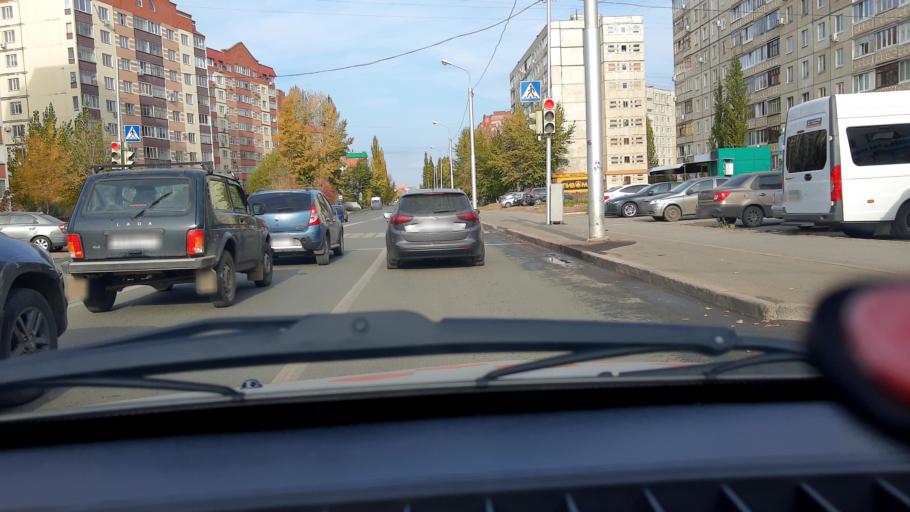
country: RU
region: Bashkortostan
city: Ufa
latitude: 54.7754
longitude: 56.0773
